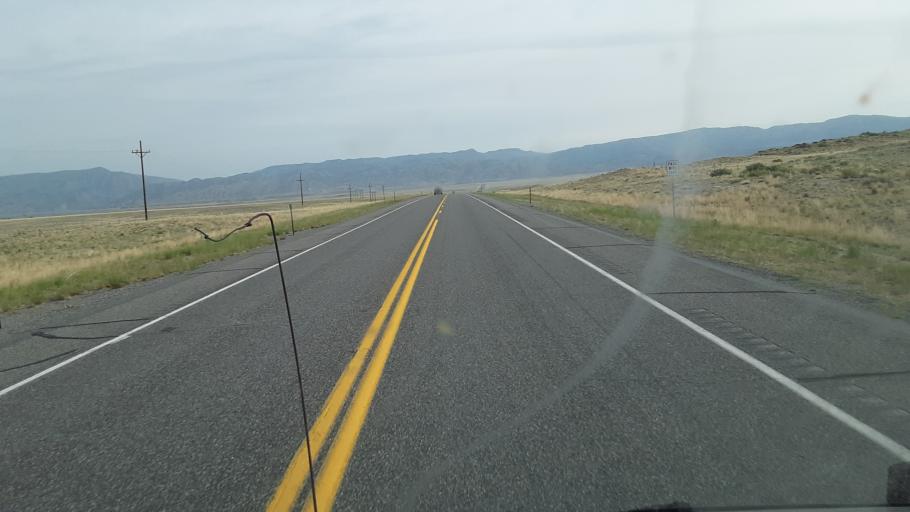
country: US
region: Wyoming
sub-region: Hot Springs County
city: Thermopolis
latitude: 43.3055
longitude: -108.1278
